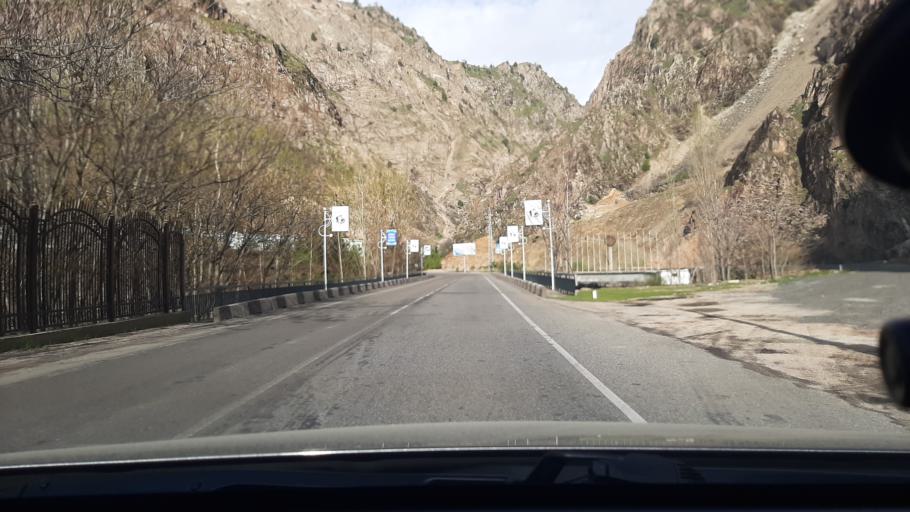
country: TJ
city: Tagob
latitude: 38.8551
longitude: 68.8468
